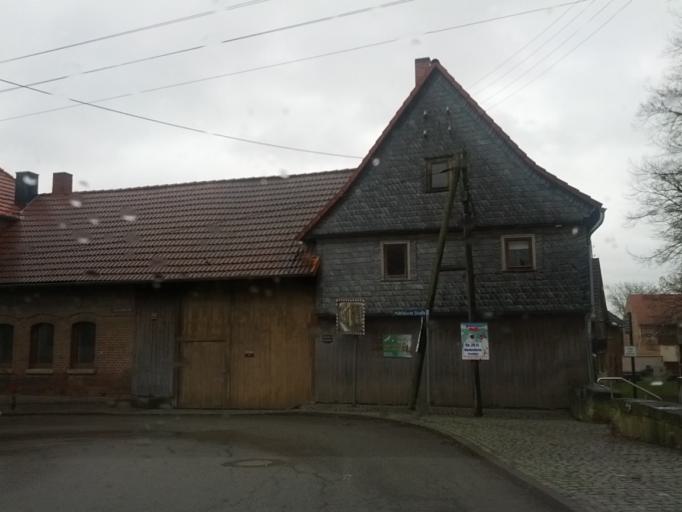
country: DE
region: Thuringia
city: Oberdorla
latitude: 51.1654
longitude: 10.4199
